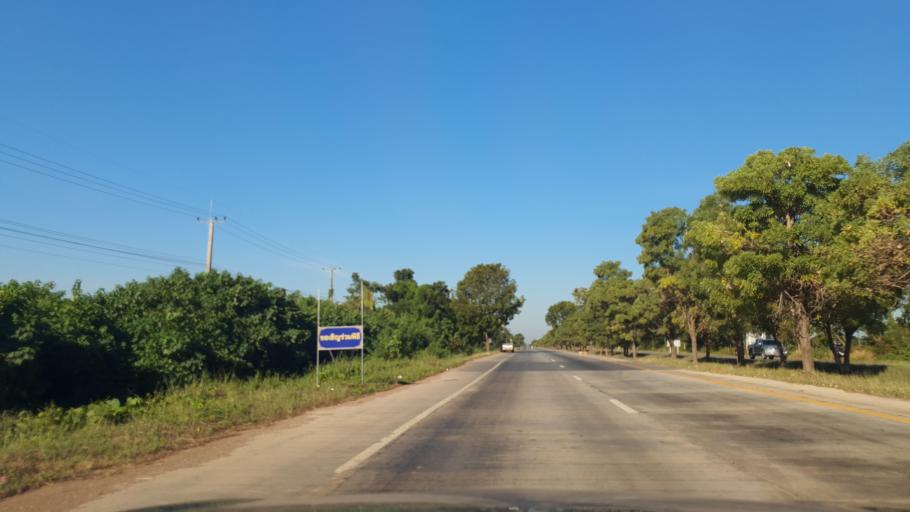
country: TH
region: Sukhothai
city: Sukhothai
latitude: 17.0647
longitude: 99.8723
